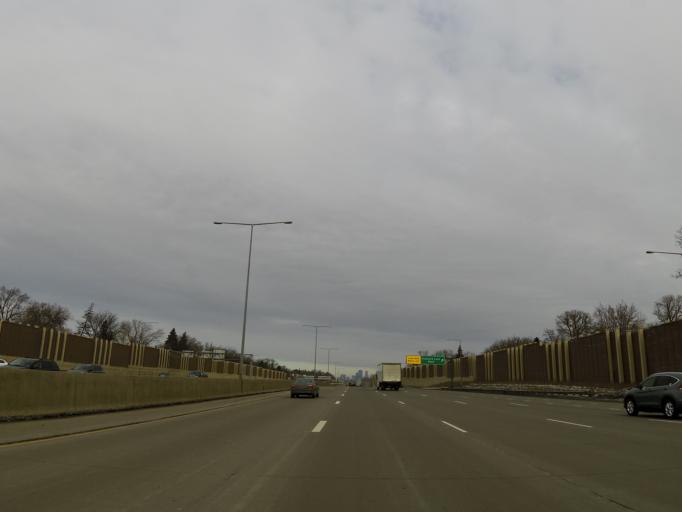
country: US
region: Minnesota
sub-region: Hennepin County
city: Richfield
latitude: 44.8980
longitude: -93.2748
